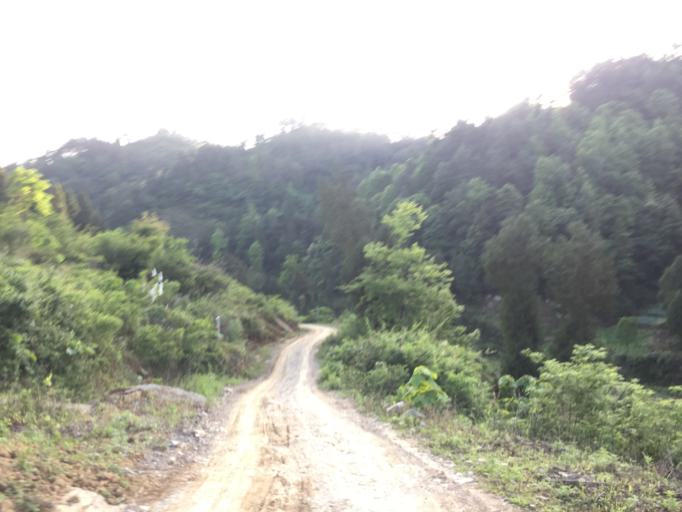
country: CN
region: Guizhou Sheng
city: Xujiaba
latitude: 27.7300
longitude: 108.0179
